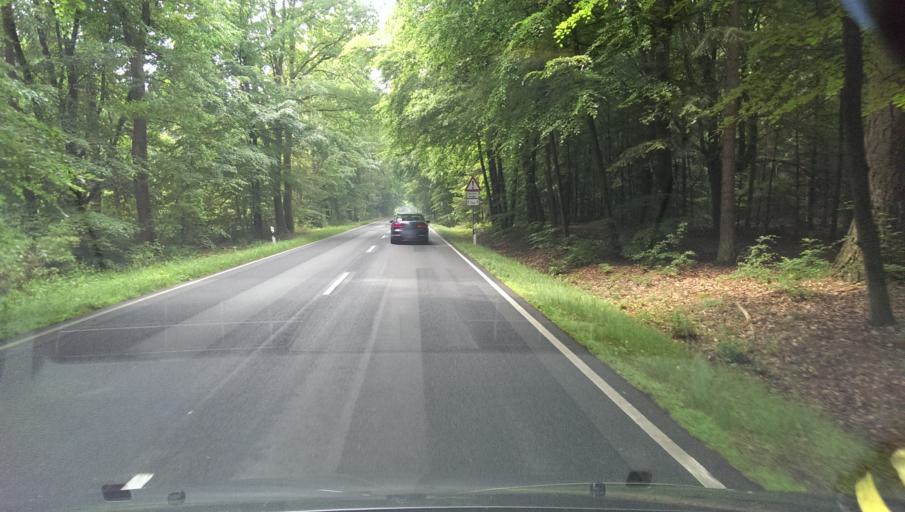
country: DE
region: Lower Saxony
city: Unterluss
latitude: 52.8263
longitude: 10.3176
